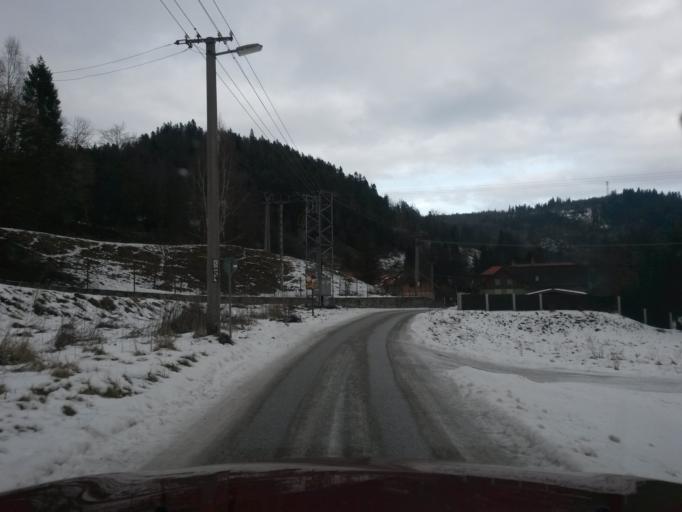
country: SK
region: Kosicky
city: Spisska Nova Ves
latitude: 48.8566
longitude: 20.5726
